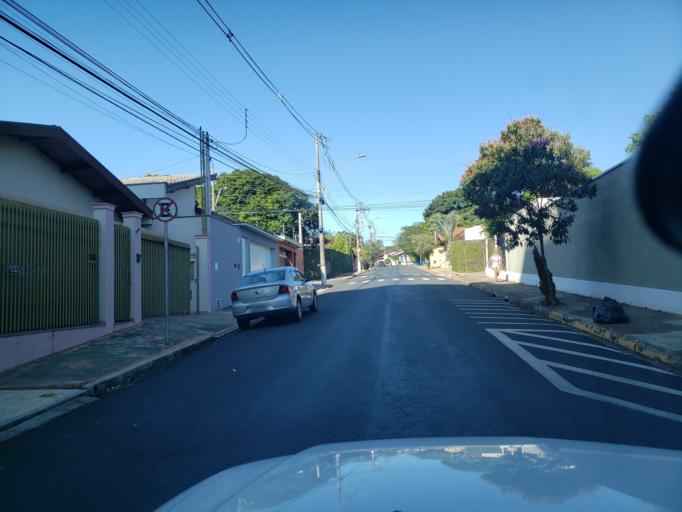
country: BR
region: Sao Paulo
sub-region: Itapira
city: Itapira
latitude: -22.4346
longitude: -46.8336
